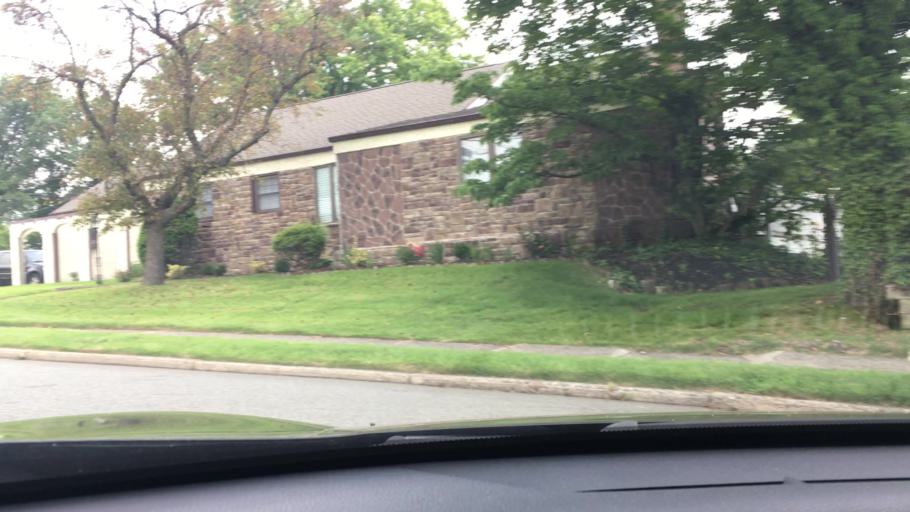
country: US
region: New Jersey
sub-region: Passaic County
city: Clifton
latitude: 40.8654
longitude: -74.1798
